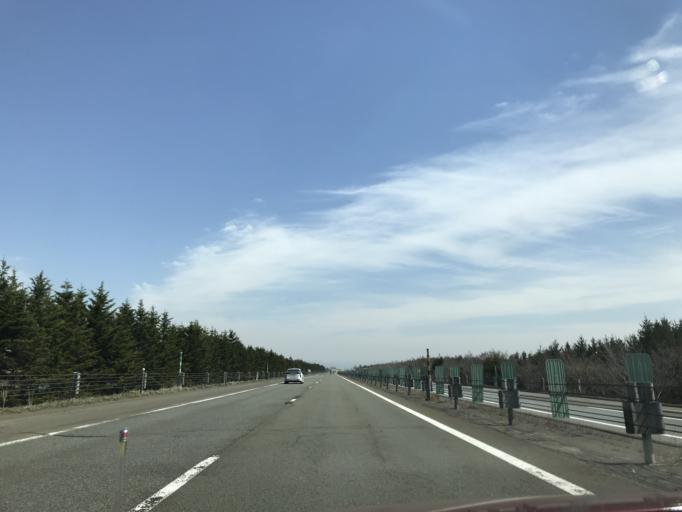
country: JP
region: Hokkaido
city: Ebetsu
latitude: 43.1271
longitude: 141.6427
